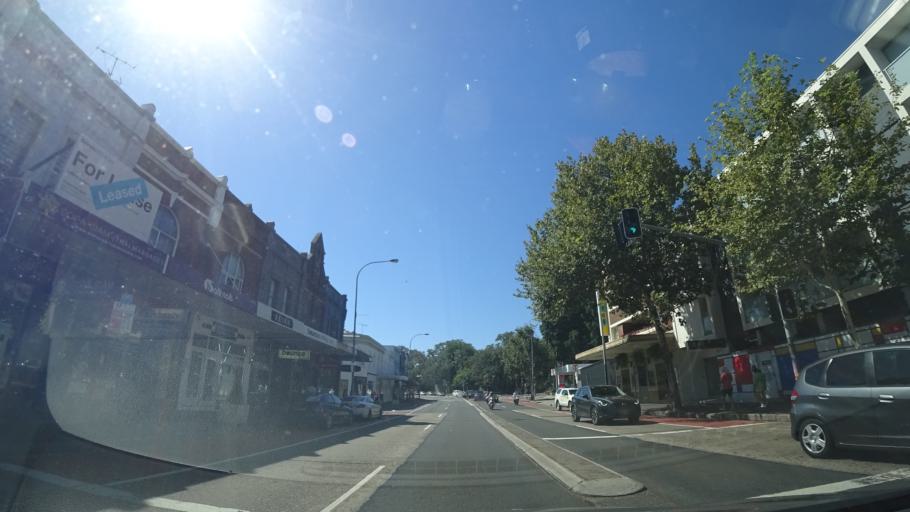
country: AU
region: New South Wales
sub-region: City of Sydney
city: Darlinghurst
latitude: -33.8826
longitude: 151.2204
